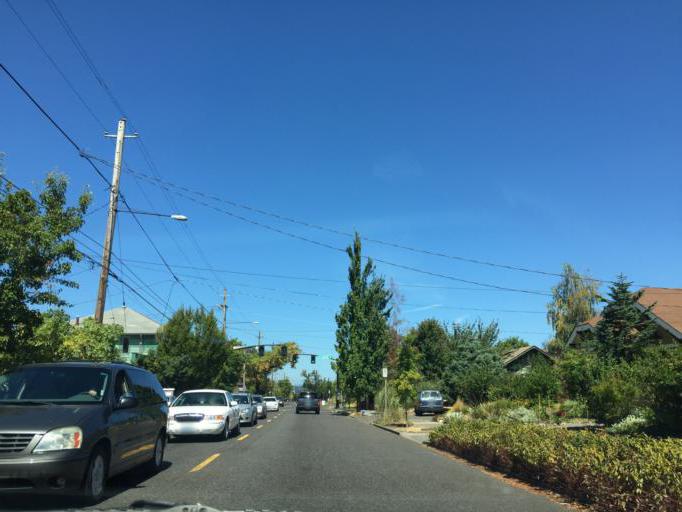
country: US
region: Oregon
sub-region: Multnomah County
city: Portland
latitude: 45.5584
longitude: -122.6307
